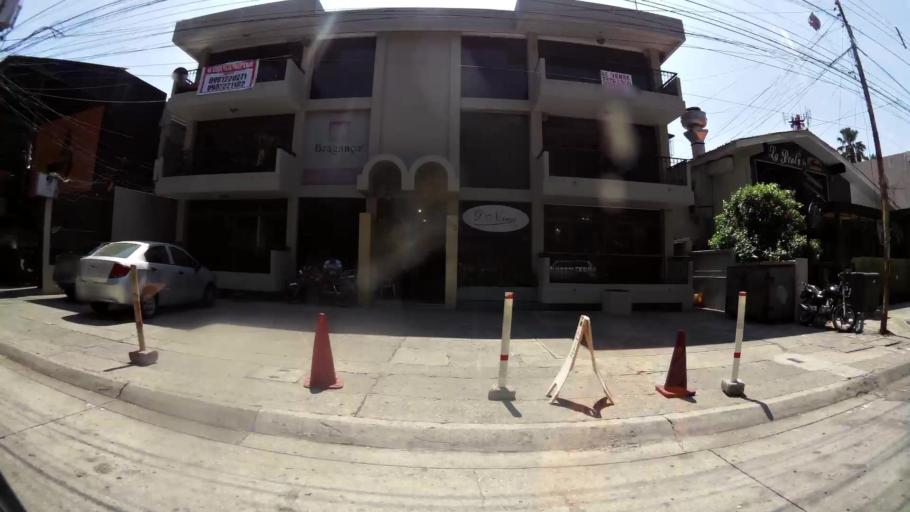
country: EC
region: Guayas
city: Guayaquil
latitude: -2.1762
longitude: -79.9054
